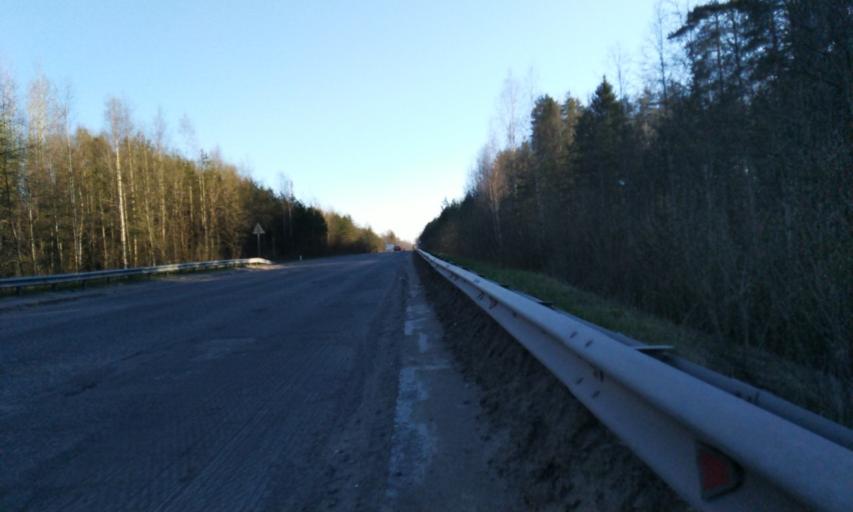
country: RU
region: Leningrad
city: Toksovo
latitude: 60.1273
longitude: 30.5173
